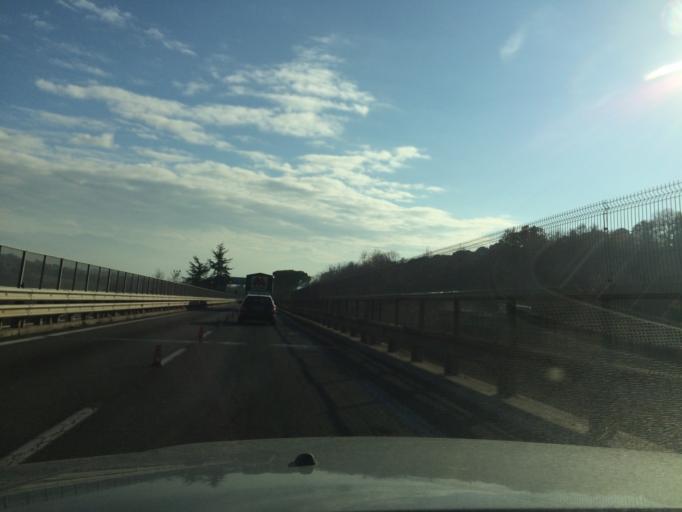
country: IT
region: Umbria
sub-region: Provincia di Terni
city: San Gemini
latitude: 42.6229
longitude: 12.5517
